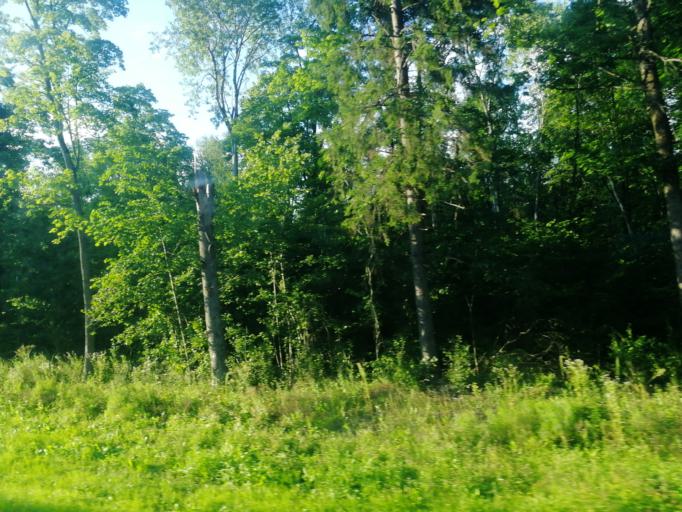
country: RU
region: Kaluga
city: Kaluga
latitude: 54.4460
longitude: 36.3146
